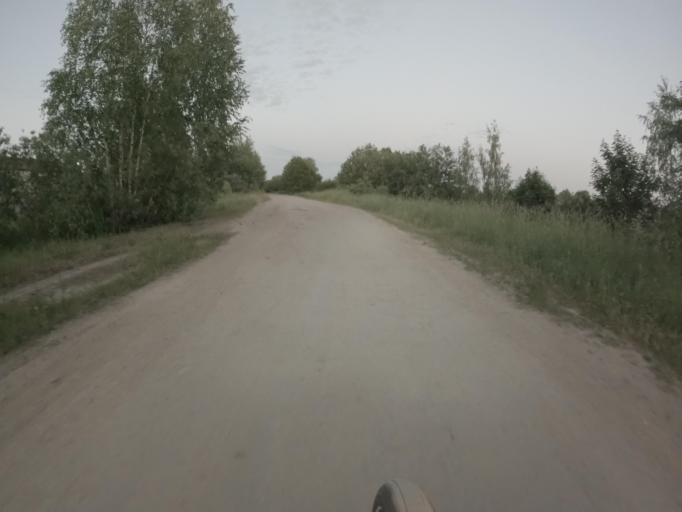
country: RU
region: St.-Petersburg
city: Sapernyy
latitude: 59.7809
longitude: 30.6638
